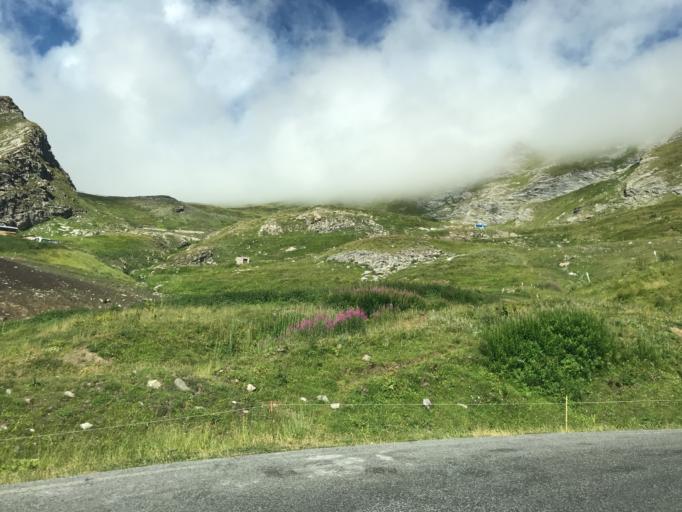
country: IT
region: Piedmont
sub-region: Provincia di Cuneo
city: Pontechianale
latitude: 44.6721
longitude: 6.9867
